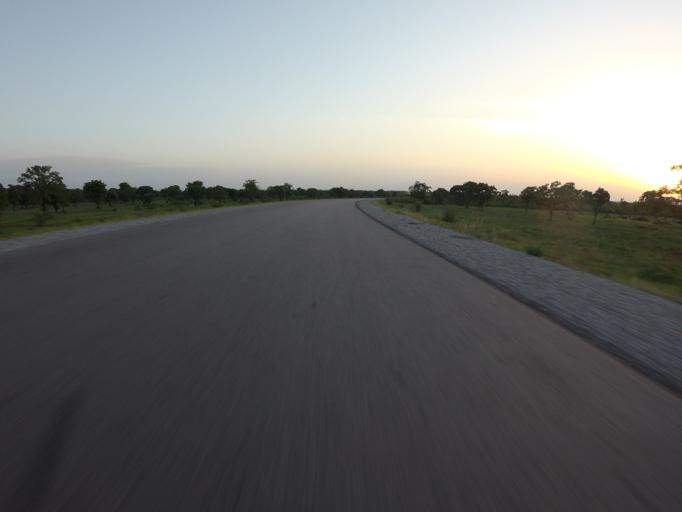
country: GH
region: Northern
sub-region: Yendi
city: Yendi
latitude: 9.9393
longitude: -0.1700
